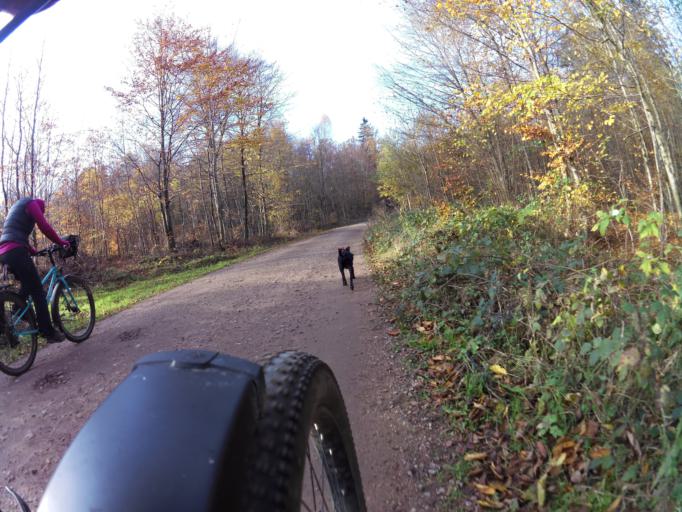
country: PL
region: Pomeranian Voivodeship
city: Strzelno
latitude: 54.7408
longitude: 18.2542
